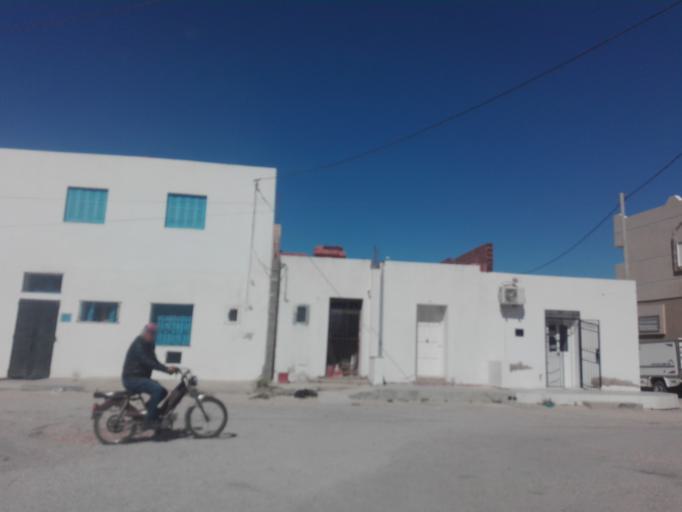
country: TN
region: Safaqis
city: Al Qarmadah
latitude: 34.7061
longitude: 11.2015
